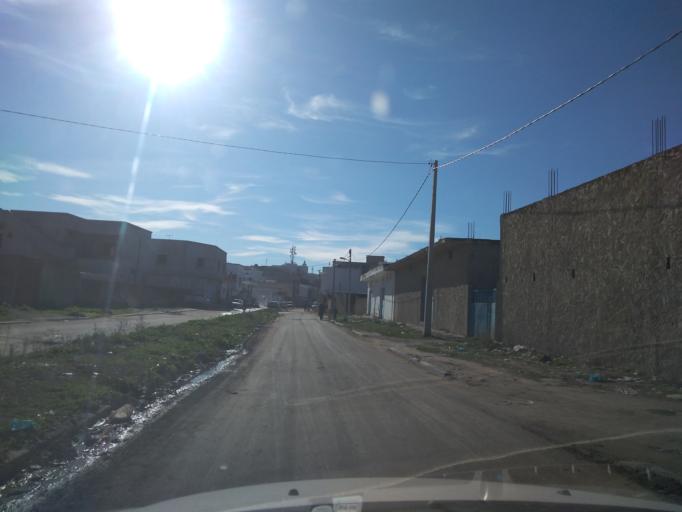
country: TN
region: Ariana
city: Qal'at al Andalus
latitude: 37.0654
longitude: 10.1199
